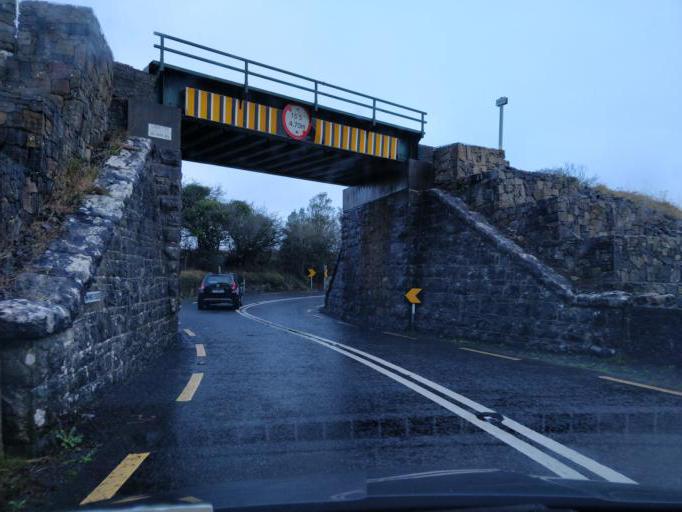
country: IE
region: Connaught
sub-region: Roscommon
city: Castlerea
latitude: 53.7662
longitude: -8.5257
